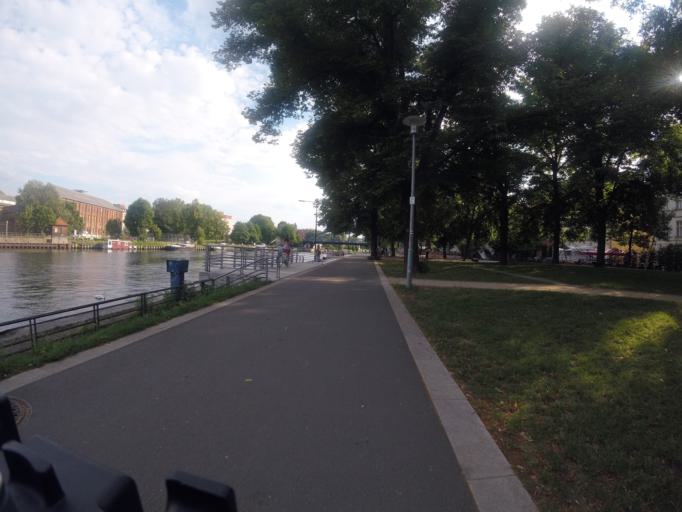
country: DE
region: Berlin
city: Spandau
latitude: 52.5366
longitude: 13.2077
